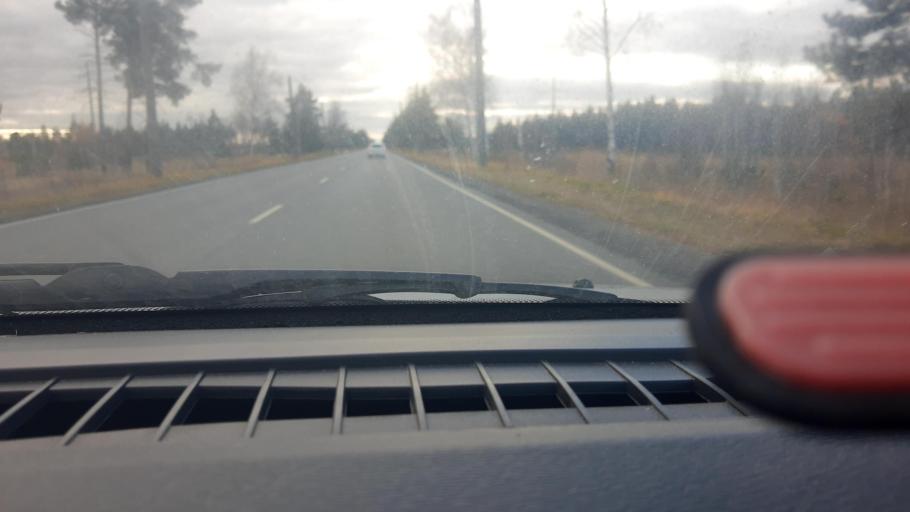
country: RU
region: Nizjnij Novgorod
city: Babino
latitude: 56.2836
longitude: 43.5778
